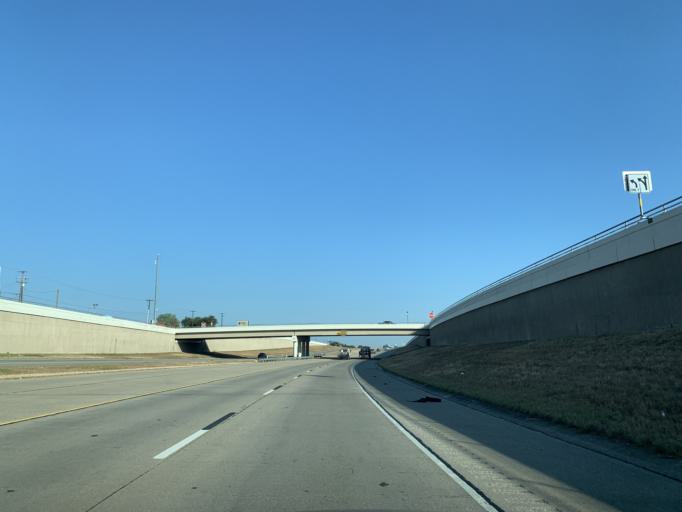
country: US
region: Texas
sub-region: Tarrant County
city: Lakeside
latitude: 32.8258
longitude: -97.4784
